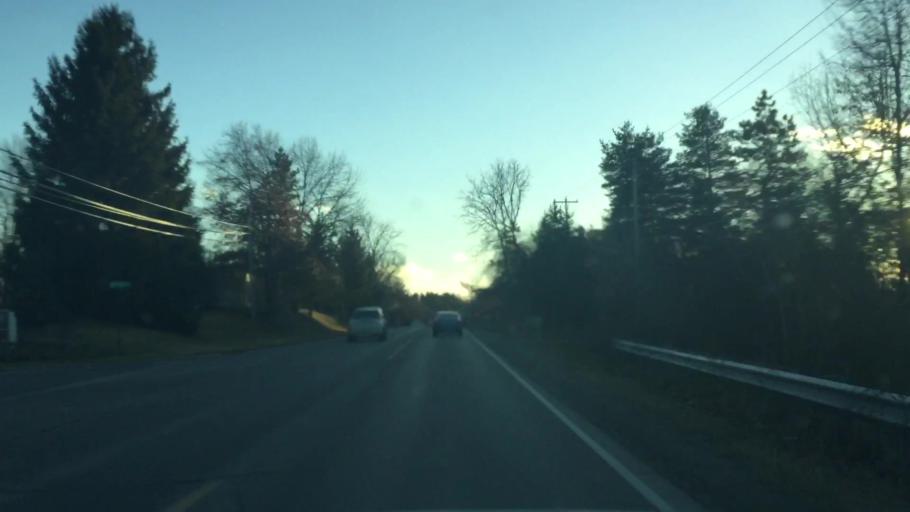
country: US
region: Michigan
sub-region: Genesee County
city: Argentine
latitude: 42.8050
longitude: -83.8200
